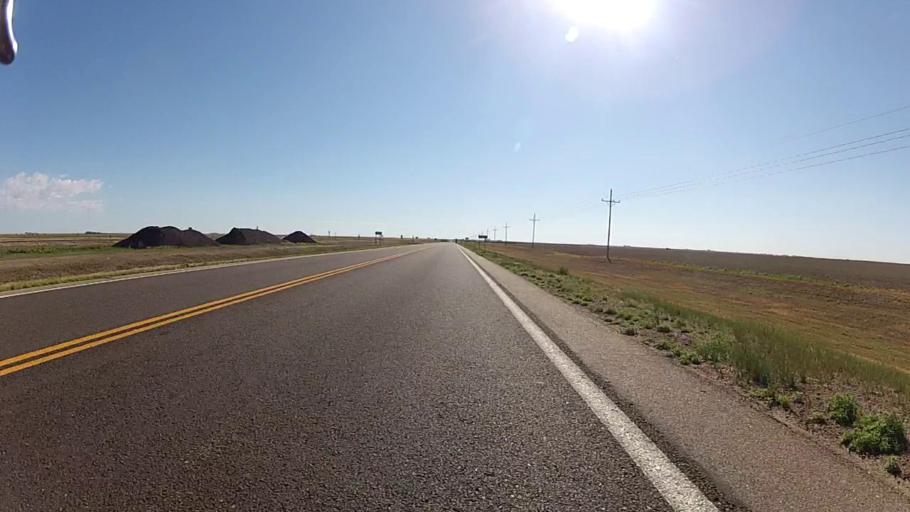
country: US
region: Kansas
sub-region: Haskell County
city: Sublette
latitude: 37.5613
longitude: -100.5665
